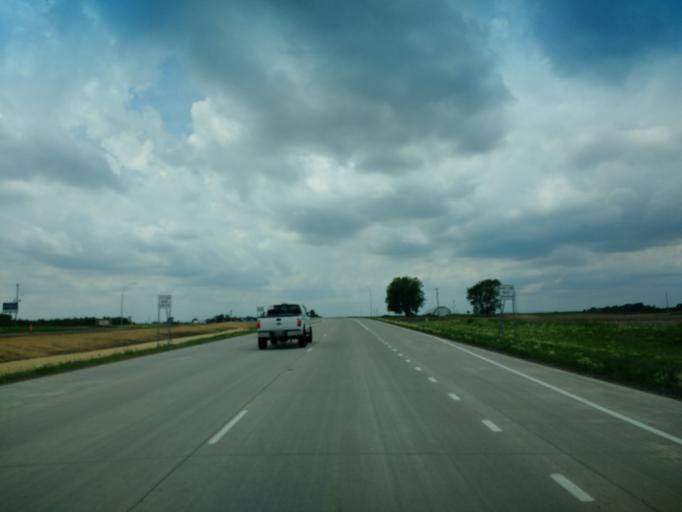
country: US
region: Minnesota
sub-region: Cottonwood County
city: Windom
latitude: 43.9102
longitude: -95.0466
